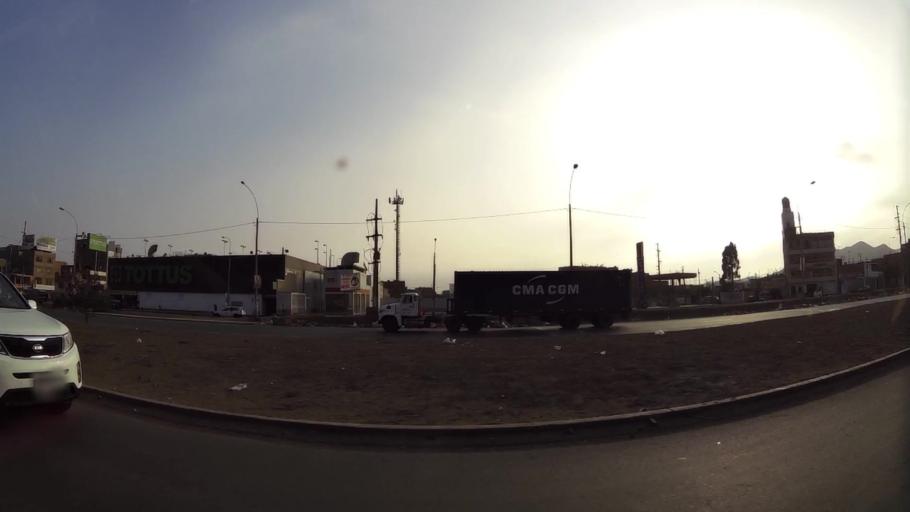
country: PE
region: Lima
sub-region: Lima
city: Independencia
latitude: -11.9542
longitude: -77.0852
